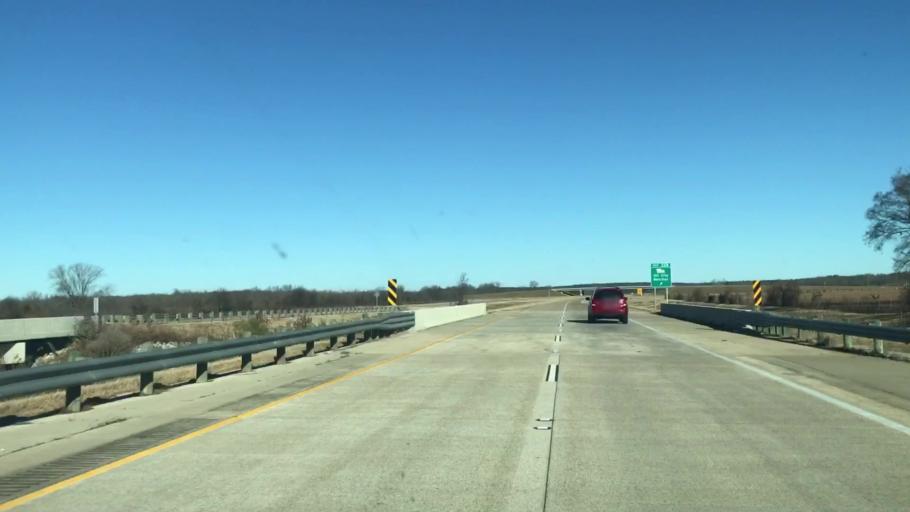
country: US
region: Louisiana
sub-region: Caddo Parish
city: Oil City
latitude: 32.7601
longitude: -93.8857
